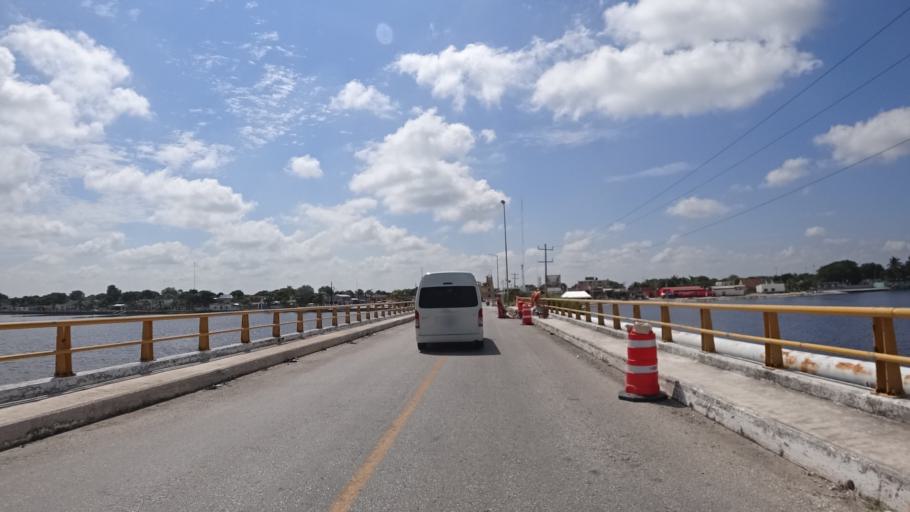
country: MX
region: Campeche
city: Sabancuy
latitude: 18.9769
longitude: -91.1815
